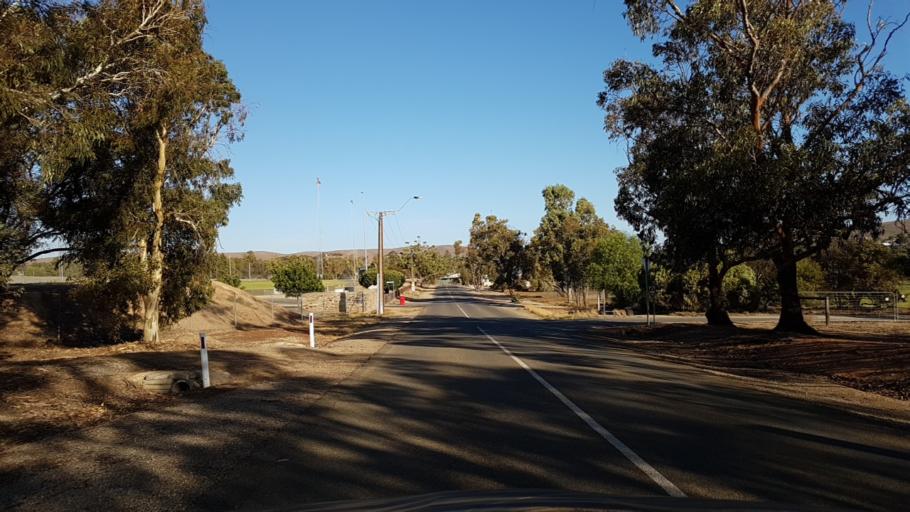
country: AU
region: South Australia
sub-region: Clare and Gilbert Valleys
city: Clare
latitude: -33.6755
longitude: 138.9395
